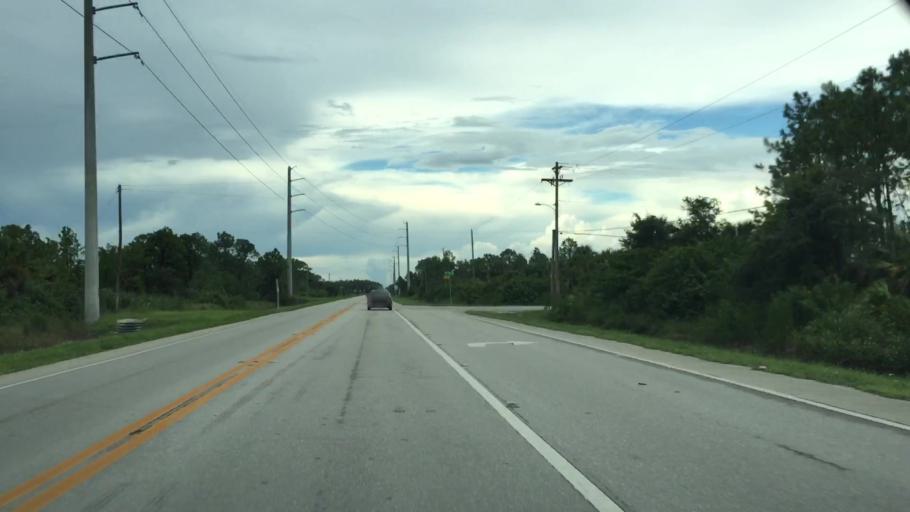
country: US
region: Florida
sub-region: Collier County
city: Orangetree
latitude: 26.3168
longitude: -81.5950
